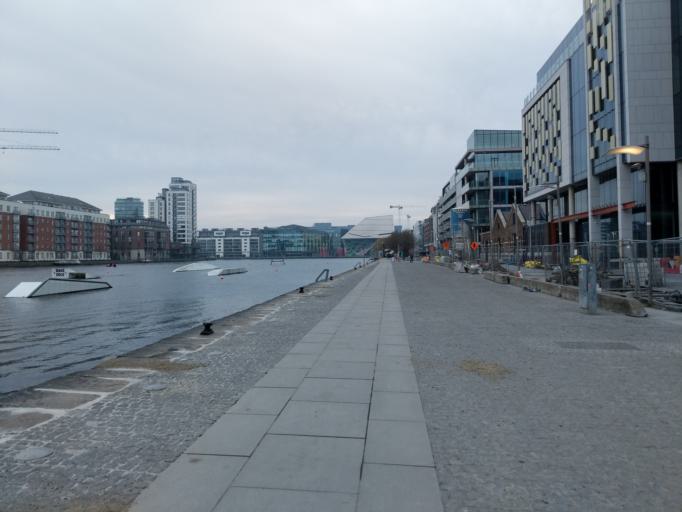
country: IE
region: Leinster
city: Ringsend
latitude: 53.3437
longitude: -6.2317
